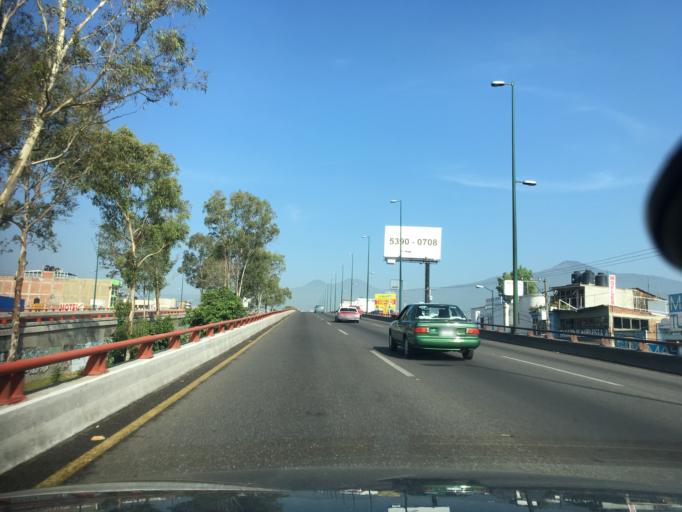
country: MX
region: Michoacan
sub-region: Tarimbaro
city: Real Hacienda (Metropolis)
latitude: 19.7262
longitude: -101.2093
